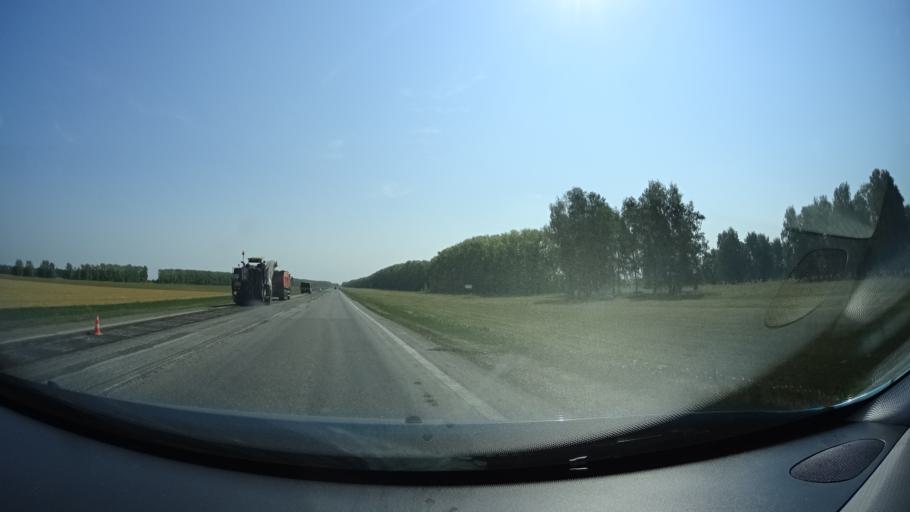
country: RU
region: Bashkortostan
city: Karmaskaly
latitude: 54.3993
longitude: 56.0970
